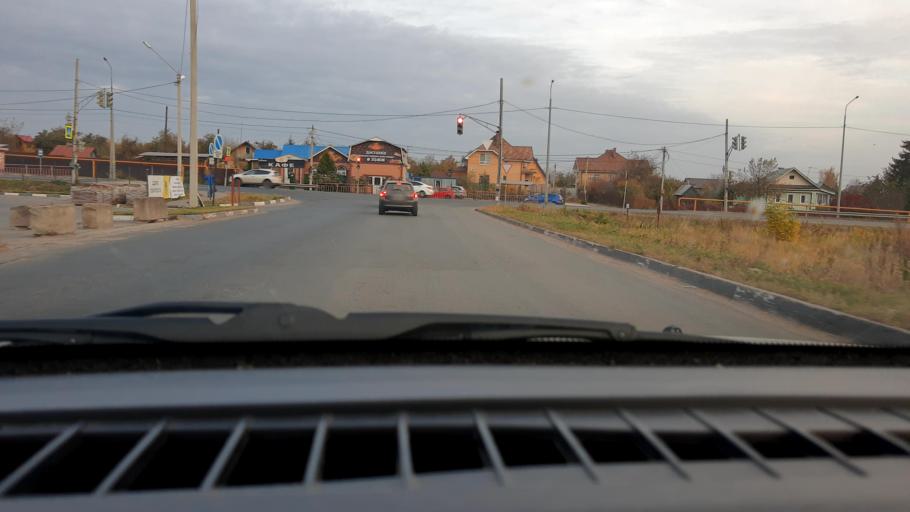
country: RU
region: Nizjnij Novgorod
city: Burevestnik
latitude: 56.2064
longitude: 43.8790
